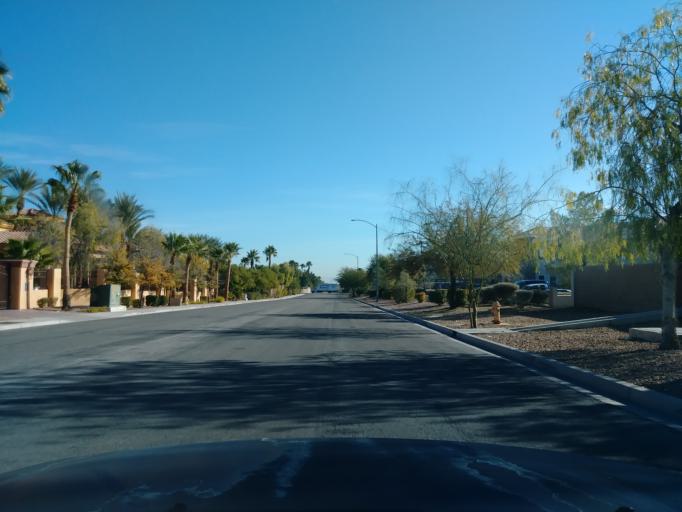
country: US
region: Nevada
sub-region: Clark County
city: Spring Valley
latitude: 36.1458
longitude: -115.2726
